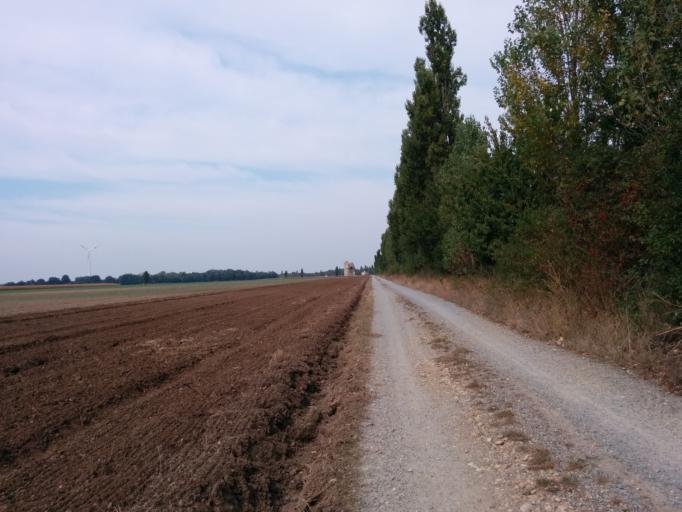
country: AT
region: Lower Austria
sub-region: Politischer Bezirk Bruck an der Leitha
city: Petronell-Carnuntum
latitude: 48.0998
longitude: 16.8575
